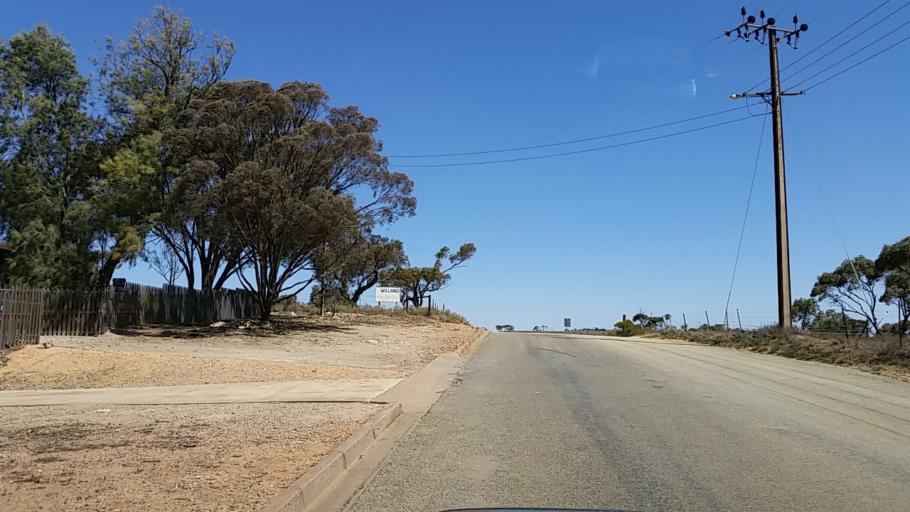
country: AU
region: South Australia
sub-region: Peterborough
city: Peterborough
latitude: -32.9818
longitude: 138.8318
